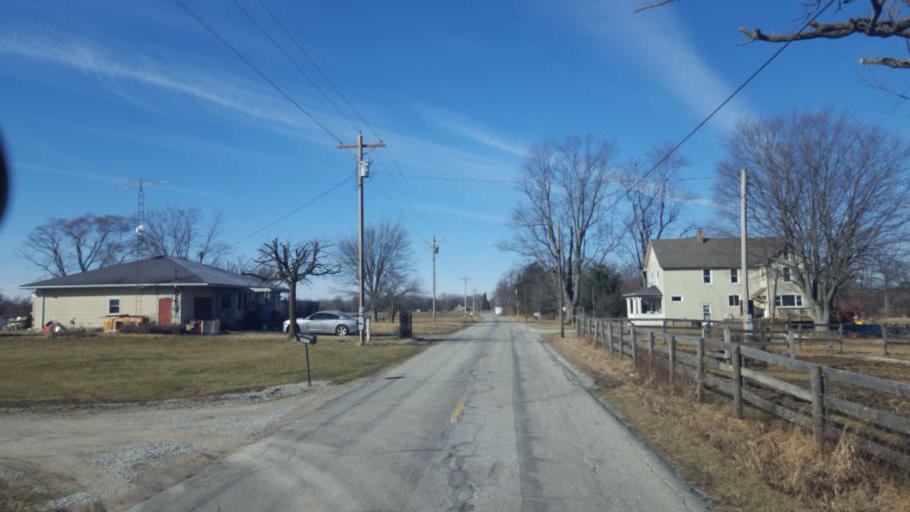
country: US
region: Ohio
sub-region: Morrow County
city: Cardington
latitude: 40.5282
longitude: -83.0026
